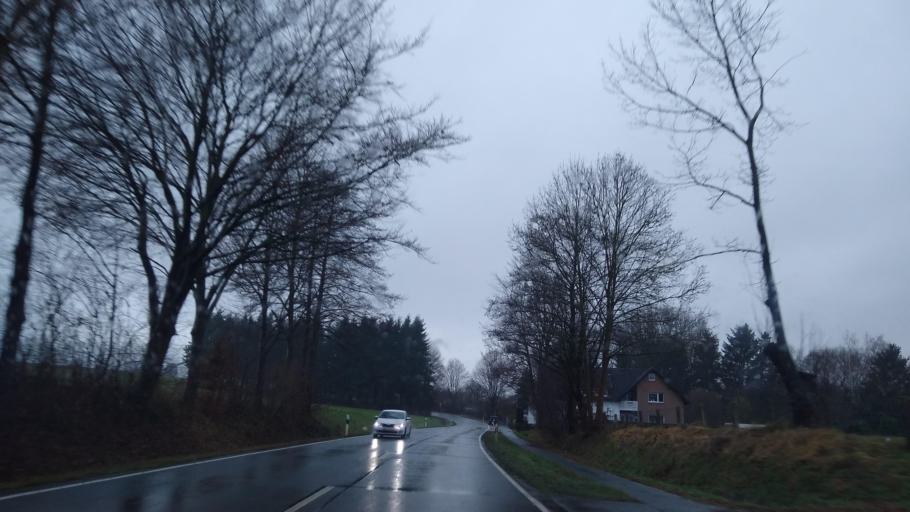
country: DE
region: North Rhine-Westphalia
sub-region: Regierungsbezirk Detmold
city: Lugde
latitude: 51.9136
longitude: 9.2790
